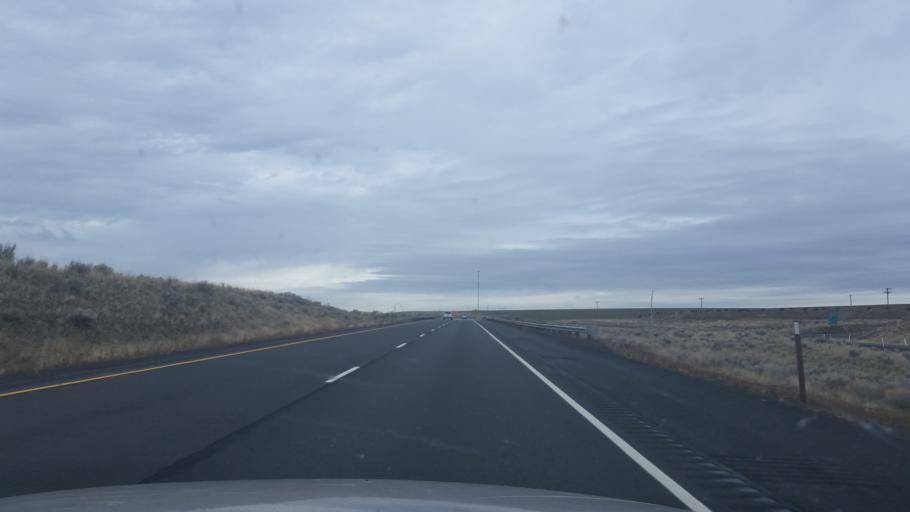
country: US
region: Washington
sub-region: Adams County
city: Ritzville
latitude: 47.0973
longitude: -118.6648
